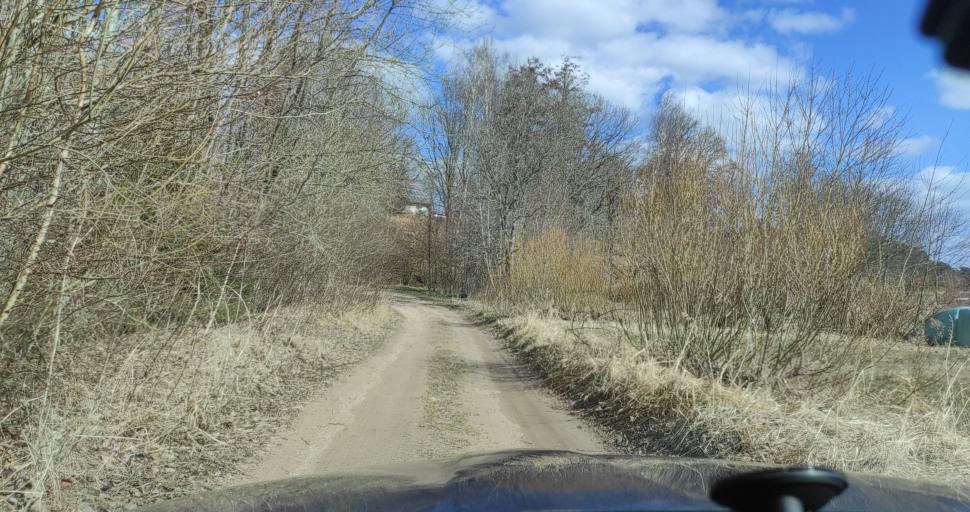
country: LV
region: Kuldigas Rajons
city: Kuldiga
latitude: 56.9587
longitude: 21.9193
